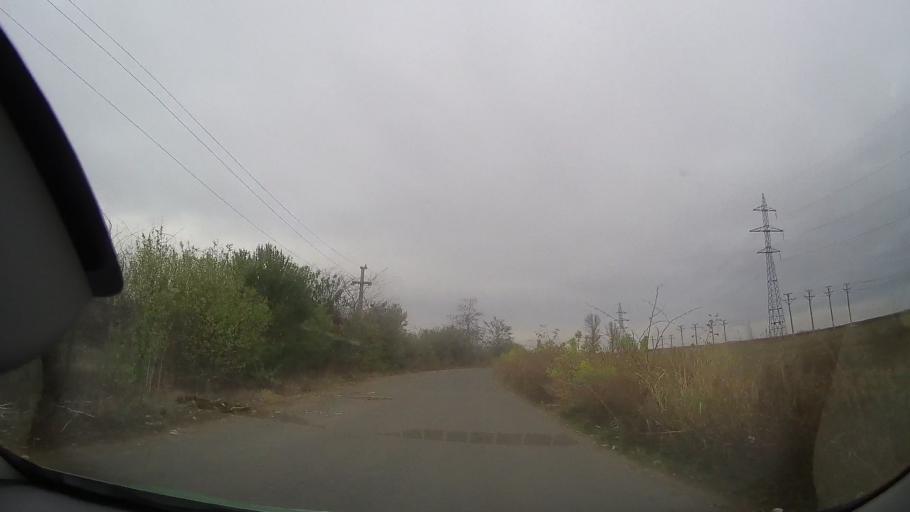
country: RO
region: Braila
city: Dudesti
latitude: 44.8959
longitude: 27.4336
